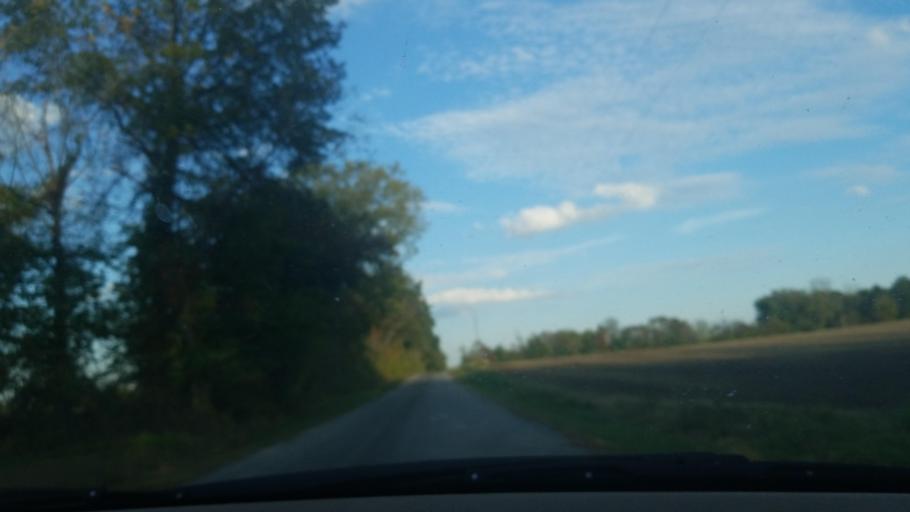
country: US
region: Illinois
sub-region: Saline County
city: Carrier Mills
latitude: 37.8050
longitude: -88.6866
